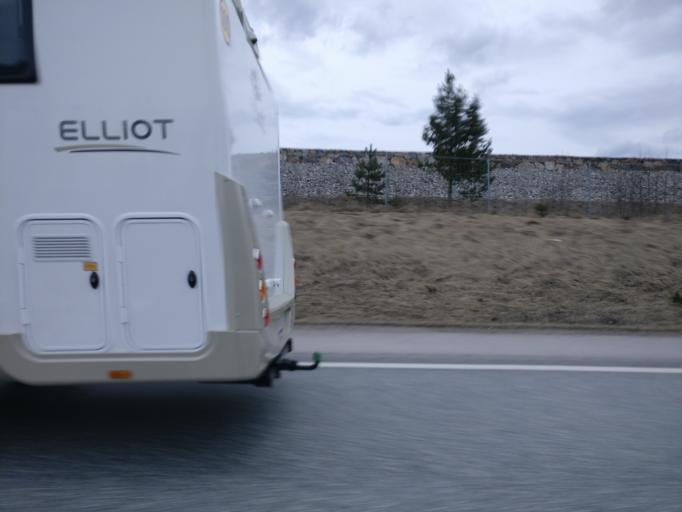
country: FI
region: Uusimaa
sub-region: Helsinki
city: Nurmijaervi
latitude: 60.4391
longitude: 24.8354
